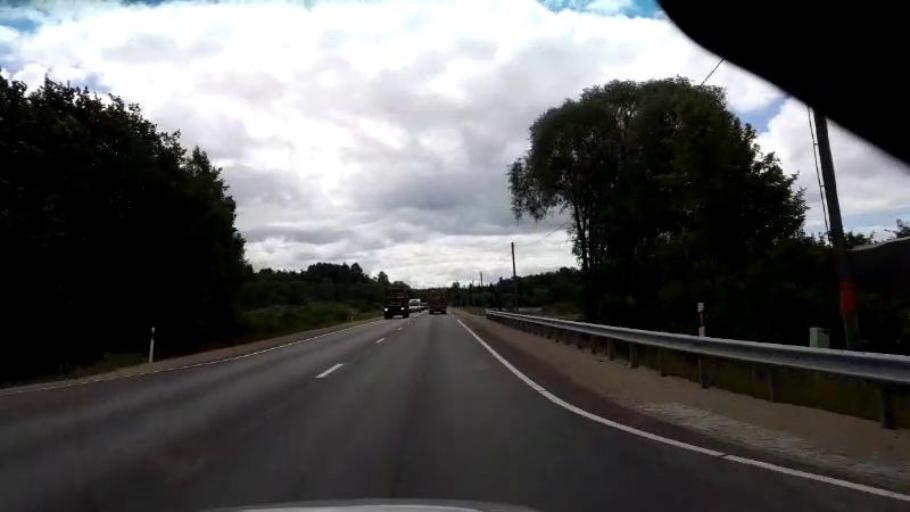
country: LV
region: Salacgrivas
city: Salacgriva
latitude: 57.7331
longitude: 24.3672
